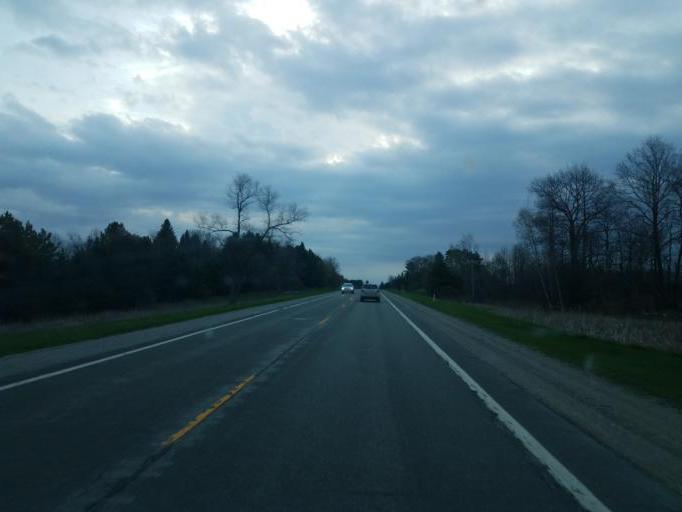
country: US
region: Michigan
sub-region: Isabella County
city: Lake Isabella
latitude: 43.5972
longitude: -84.9330
